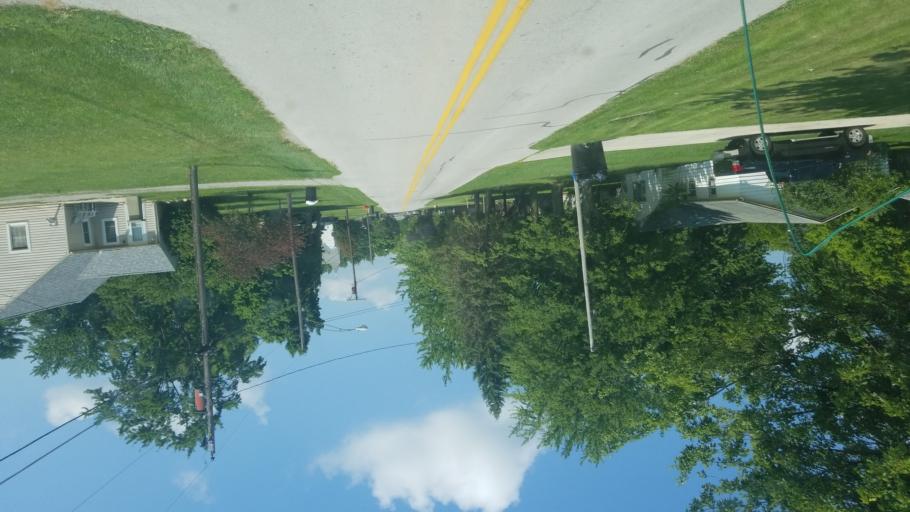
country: US
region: Ohio
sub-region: Hardin County
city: Ada
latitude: 40.7033
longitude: -83.9211
